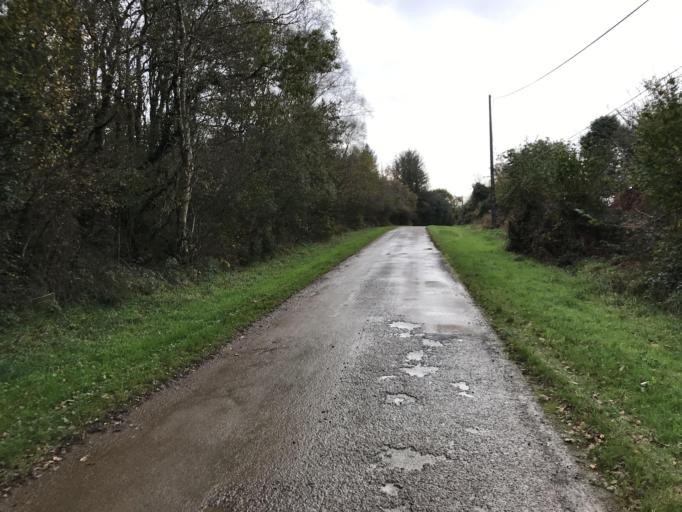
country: FR
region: Brittany
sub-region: Departement du Finistere
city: Irvillac
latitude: 48.3565
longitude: -4.2121
